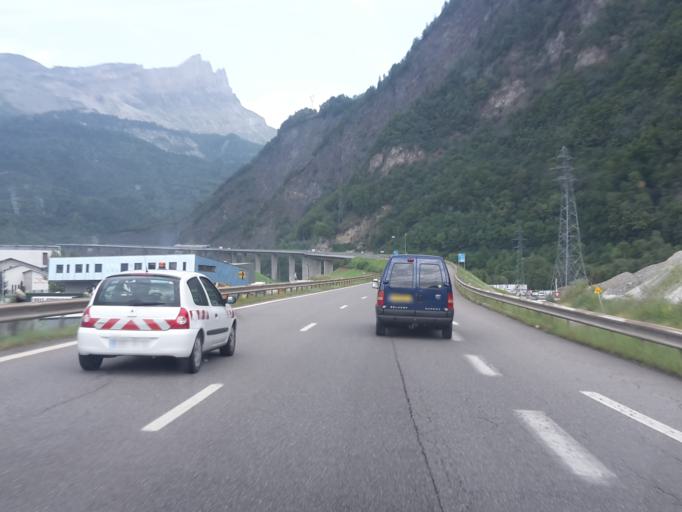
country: FR
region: Rhone-Alpes
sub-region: Departement de la Haute-Savoie
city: Saint-Gervais-les-Bains
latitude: 45.9178
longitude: 6.7246
